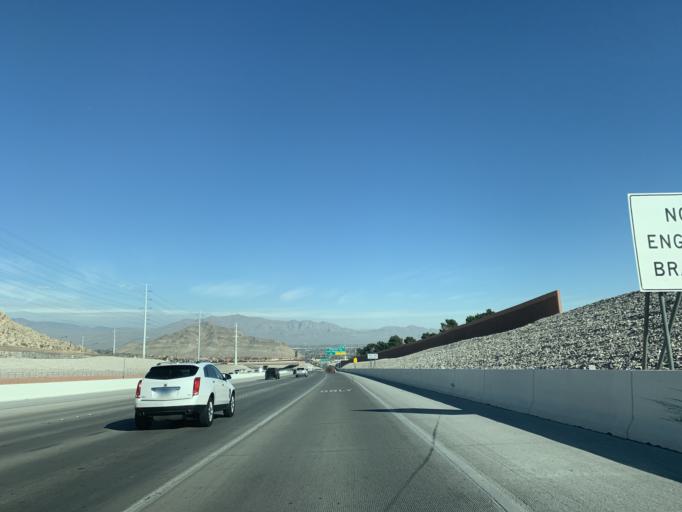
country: US
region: Nevada
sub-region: Clark County
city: Summerlin South
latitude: 36.2140
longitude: -115.3325
